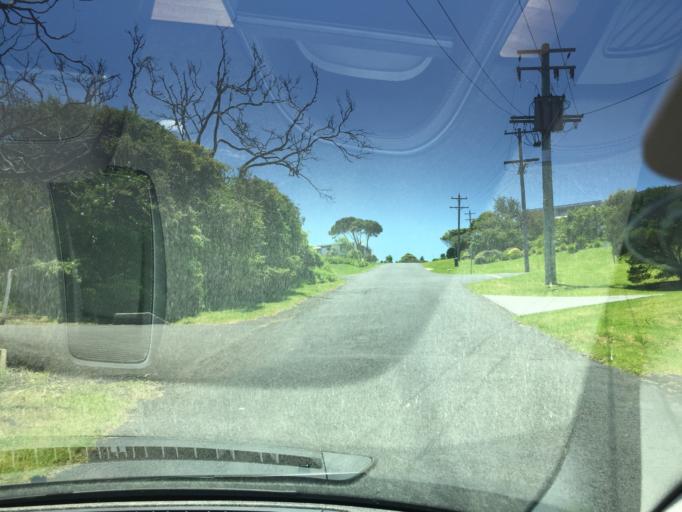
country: AU
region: New South Wales
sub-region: Bega Valley
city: Merimbula
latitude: -36.8969
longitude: 149.9266
